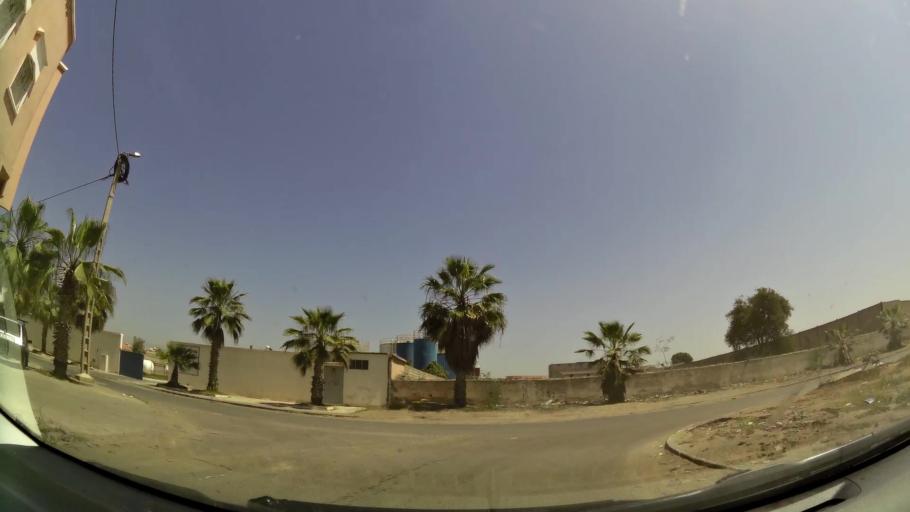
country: MA
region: Souss-Massa-Draa
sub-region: Inezgane-Ait Mellou
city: Inezgane
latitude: 30.3390
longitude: -9.4866
